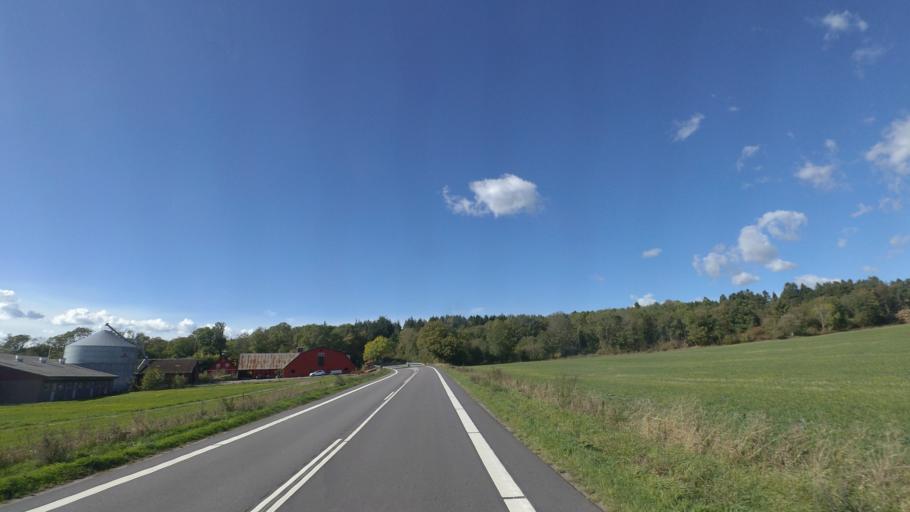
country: DK
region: Capital Region
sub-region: Bornholm Kommune
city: Akirkeby
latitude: 55.0641
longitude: 15.0222
